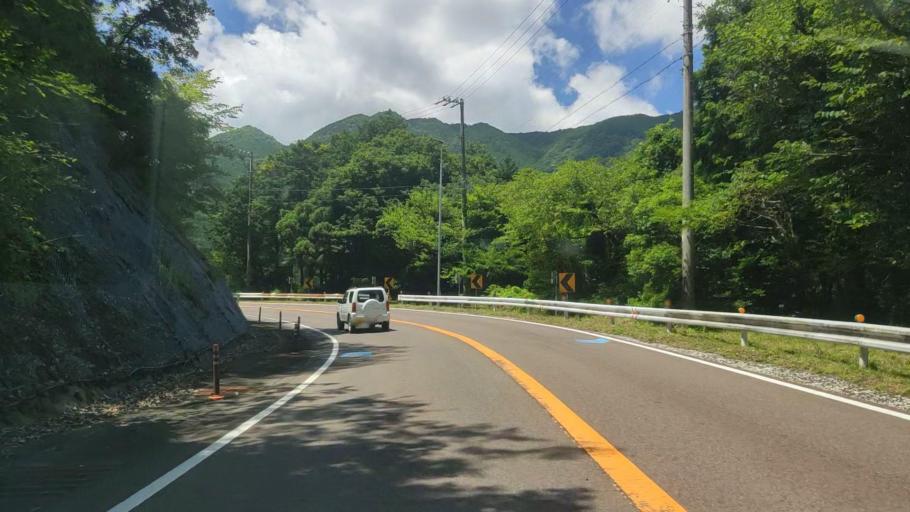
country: JP
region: Mie
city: Owase
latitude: 34.1027
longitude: 136.2041
